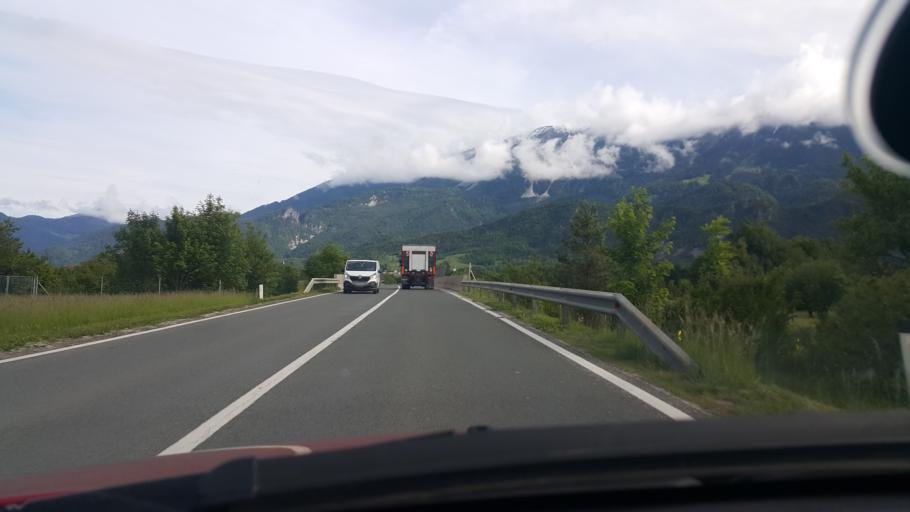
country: SI
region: Radovljica
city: Lesce
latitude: 46.3796
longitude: 14.1497
